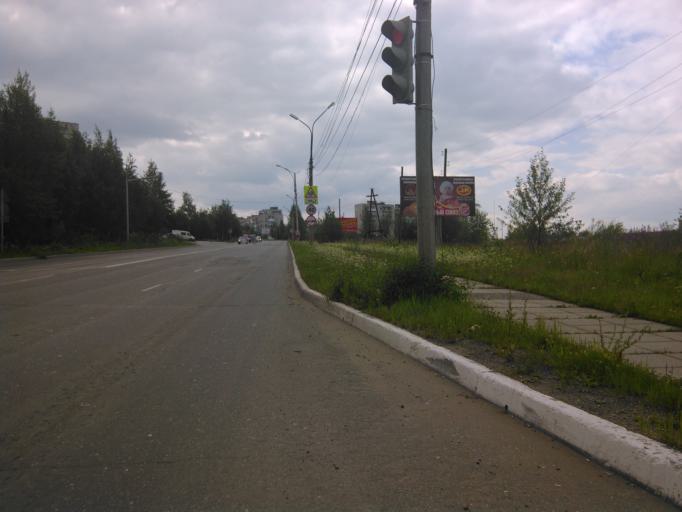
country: RU
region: Sverdlovsk
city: Krasnotur'insk
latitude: 59.7594
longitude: 60.1731
